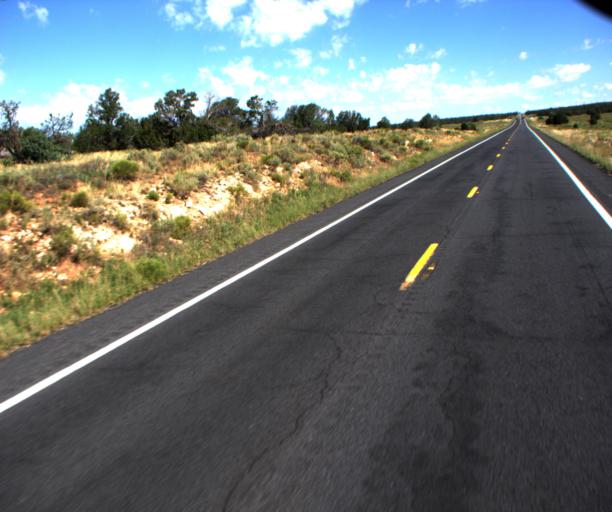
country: US
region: Arizona
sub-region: Coconino County
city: Grand Canyon Village
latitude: 35.7958
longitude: -112.1304
